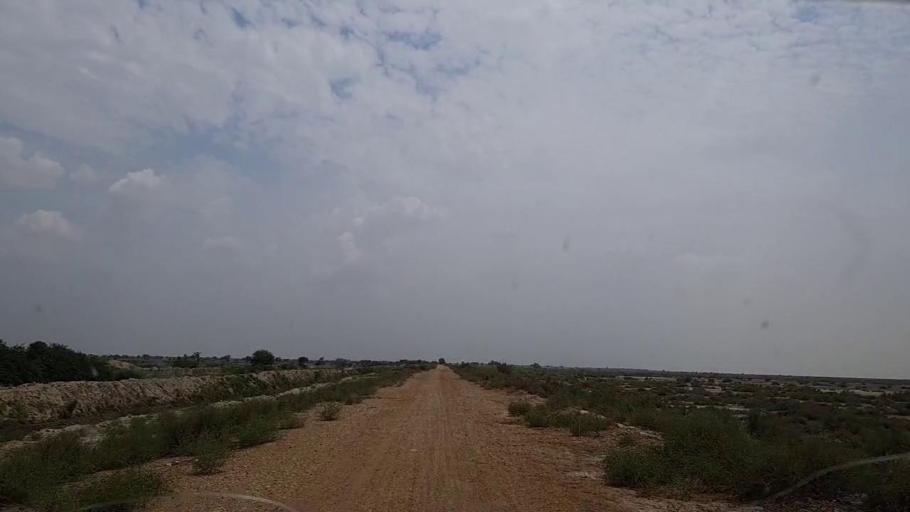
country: PK
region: Sindh
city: Phulji
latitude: 26.8383
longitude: 67.6179
